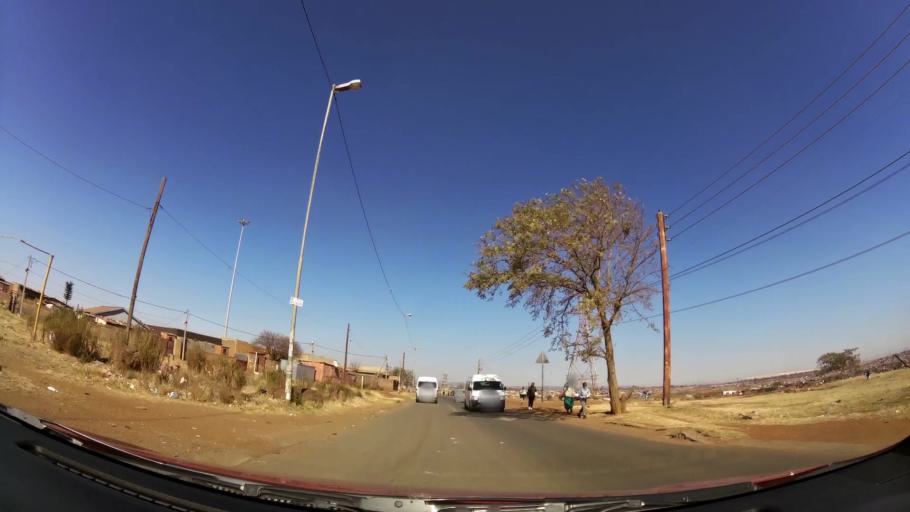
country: ZA
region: Gauteng
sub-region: City of Johannesburg Metropolitan Municipality
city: Soweto
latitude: -26.2219
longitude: 27.8200
